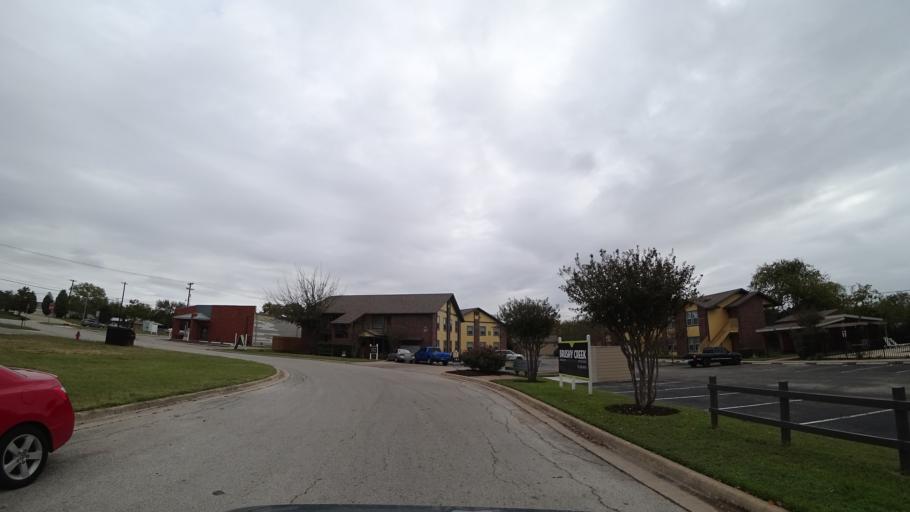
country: US
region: Texas
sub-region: Williamson County
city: Round Rock
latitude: 30.5163
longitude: -97.6934
